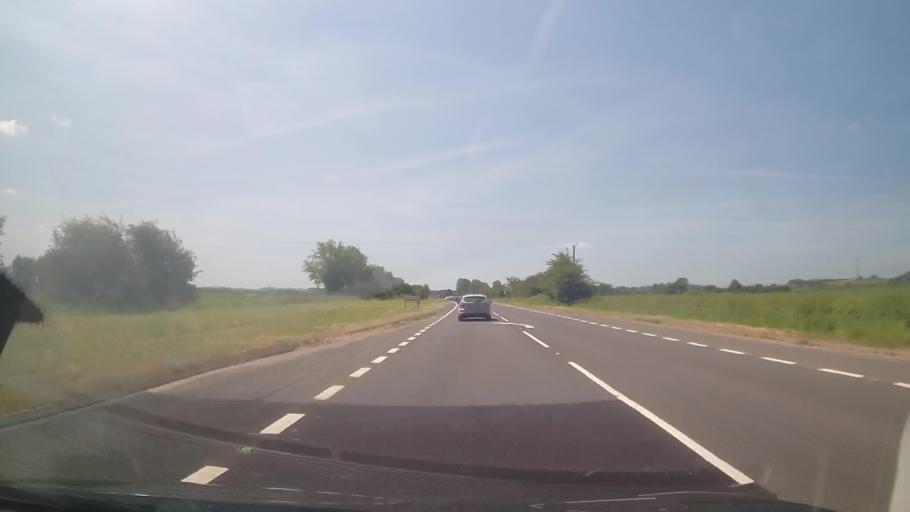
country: GB
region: England
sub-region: Herefordshire
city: Wellington
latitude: 52.1383
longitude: -2.7293
